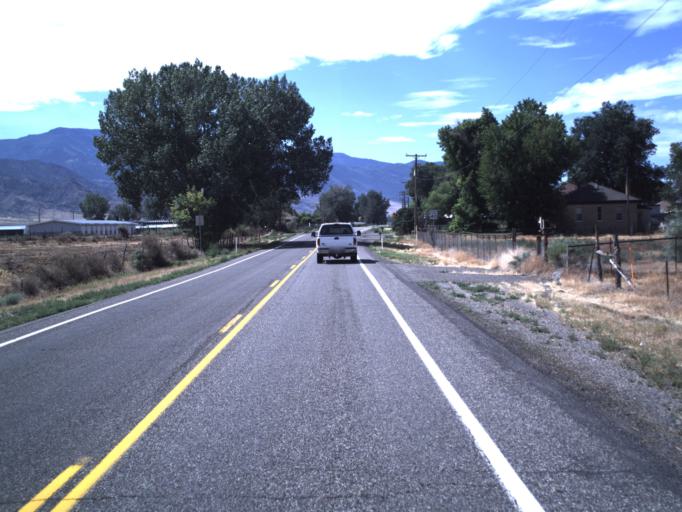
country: US
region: Utah
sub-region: Sevier County
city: Monroe
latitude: 38.6755
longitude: -112.1211
